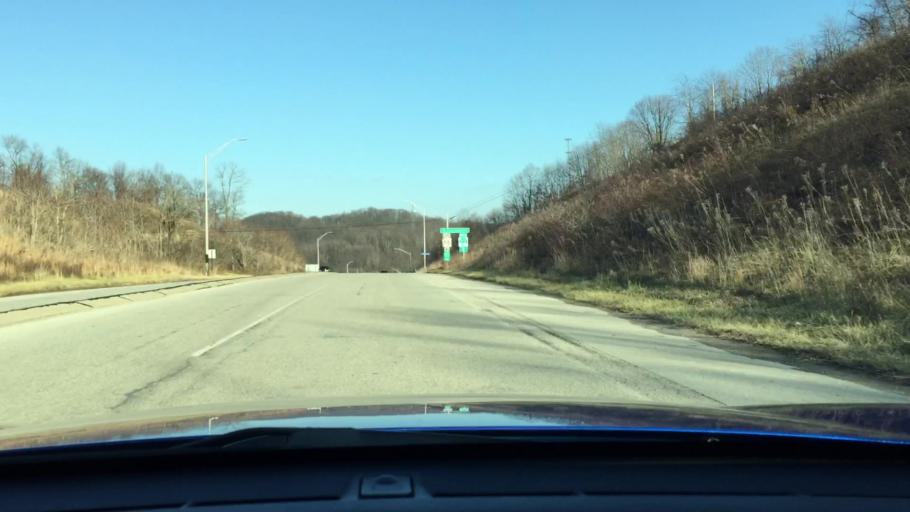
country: US
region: Pennsylvania
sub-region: Westmoreland County
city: New Stanton
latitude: 40.2311
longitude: -79.6051
